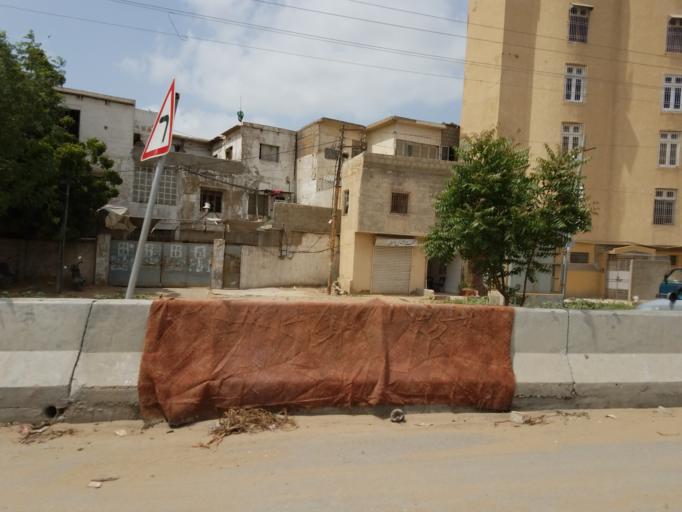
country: PK
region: Sindh
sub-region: Karachi District
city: Karachi
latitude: 24.9326
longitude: 67.0896
